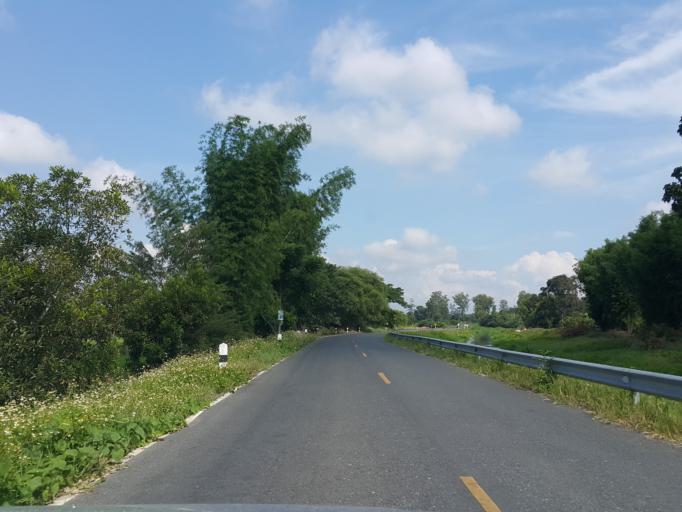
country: TH
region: Chiang Mai
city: San Sai
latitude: 18.9629
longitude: 98.9927
